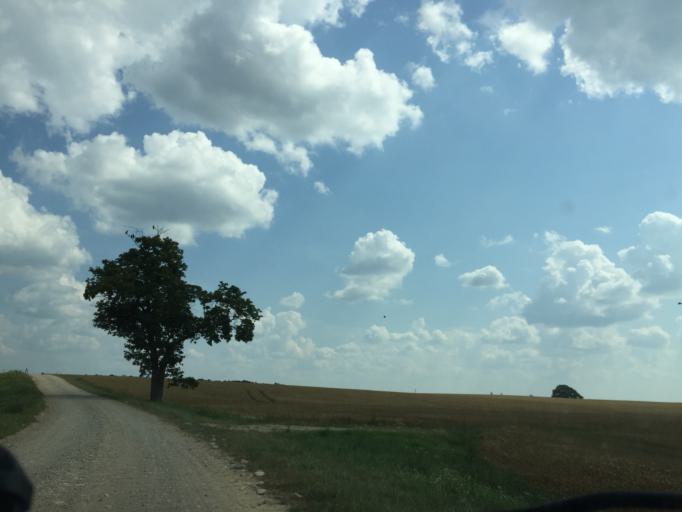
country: LT
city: Zagare
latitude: 56.3284
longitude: 23.0902
